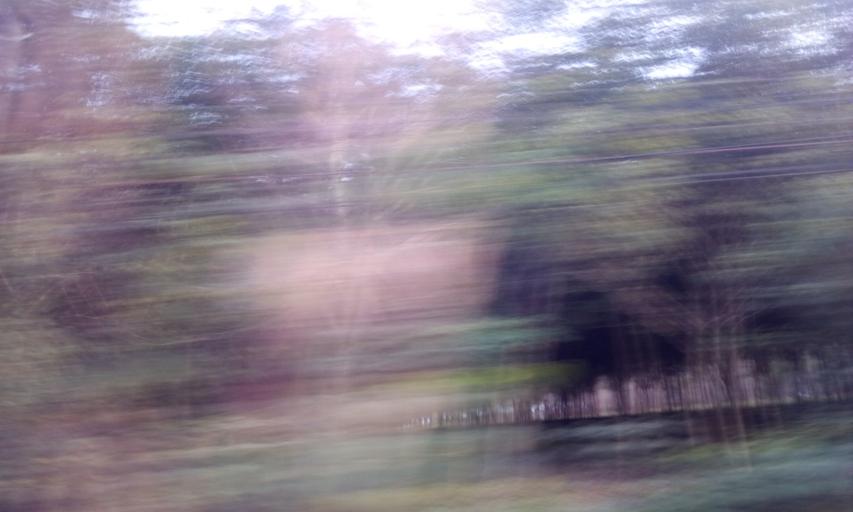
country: TH
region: Trat
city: Laem Ngop
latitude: 12.2596
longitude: 102.2907
